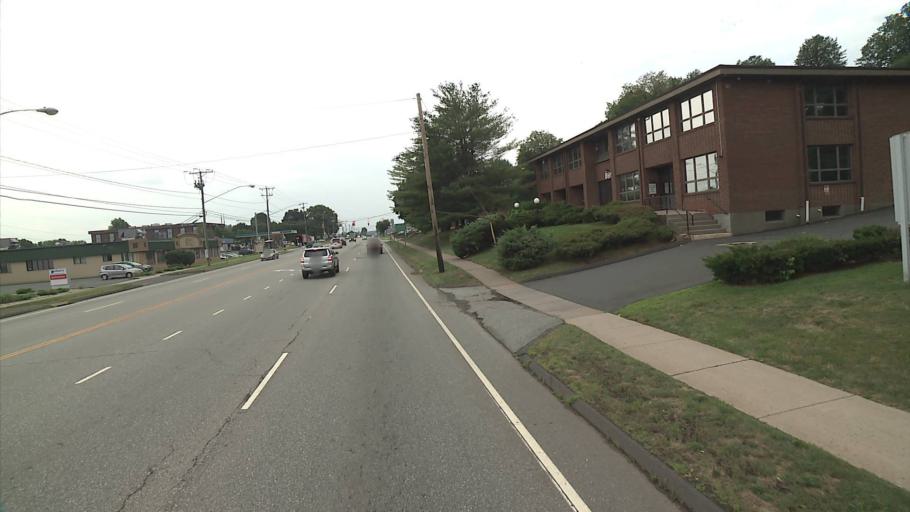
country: US
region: Connecticut
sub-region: Hartford County
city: Wethersfield
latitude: 41.6991
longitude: -72.6589
